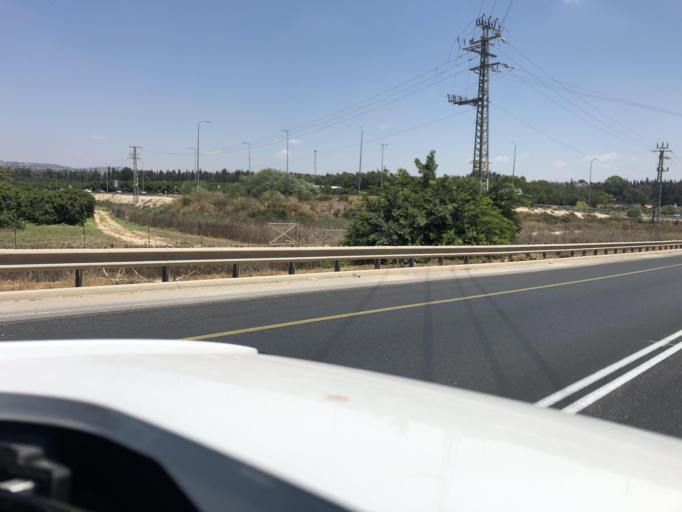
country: IL
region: Central District
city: Jaljulya
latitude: 32.1403
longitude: 34.9618
